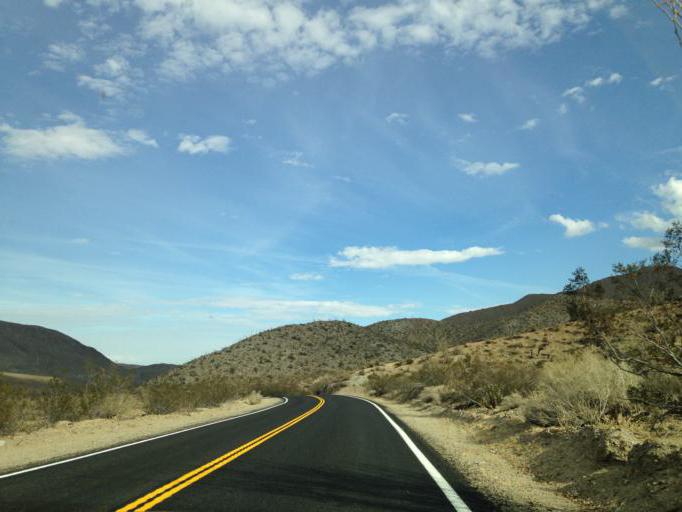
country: US
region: California
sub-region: San Diego County
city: Borrego Springs
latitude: 33.1311
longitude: -116.4057
